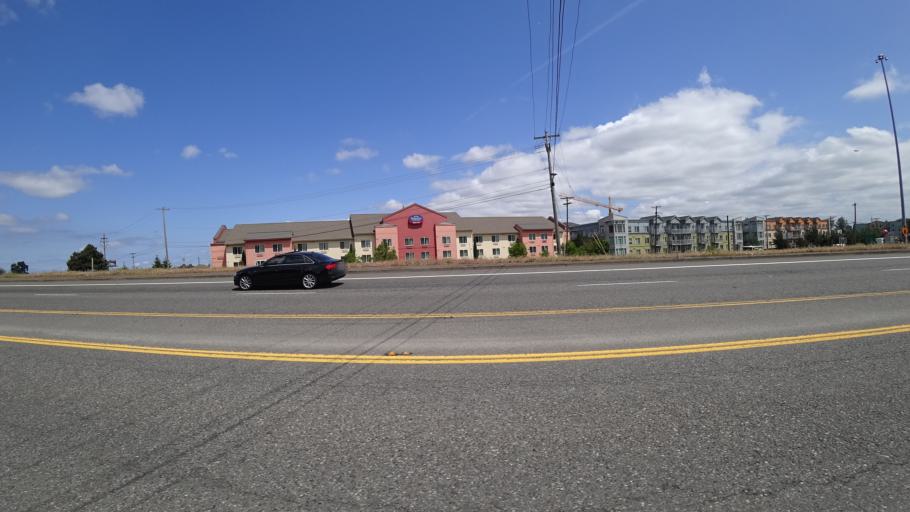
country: US
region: Washington
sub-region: Clark County
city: Vancouver
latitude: 45.6030
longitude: -122.6800
